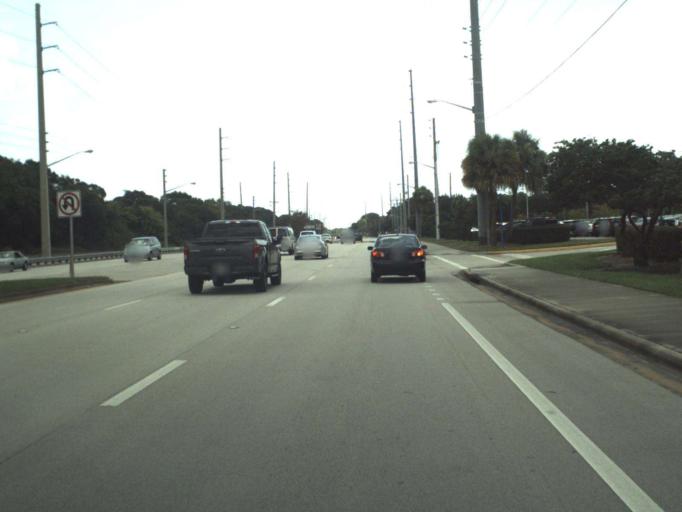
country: US
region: Florida
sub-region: Saint Lucie County
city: Fort Pierce South
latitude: 27.4254
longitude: -80.3583
